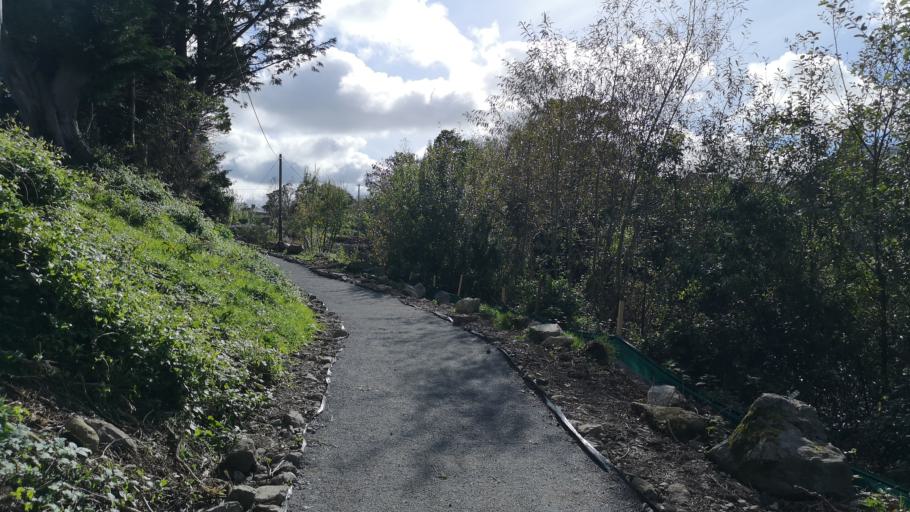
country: IE
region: Connaught
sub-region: County Galway
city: Gort
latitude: 53.0685
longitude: -8.8168
